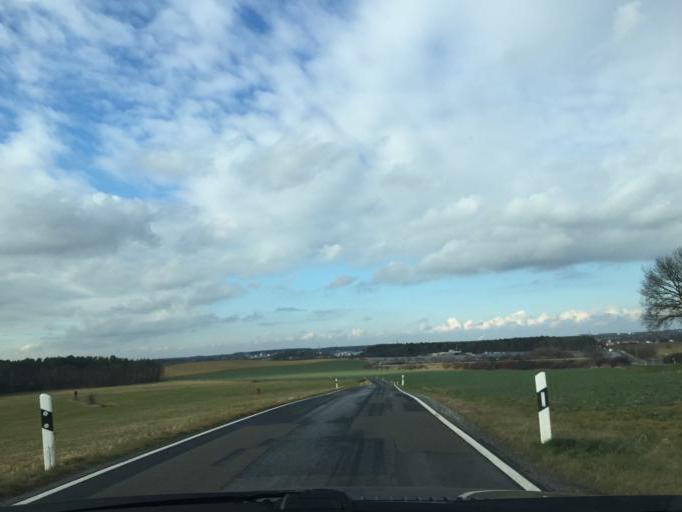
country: DE
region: Saxony
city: Ottendorf-Okrilla
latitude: 51.1677
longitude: 13.8617
